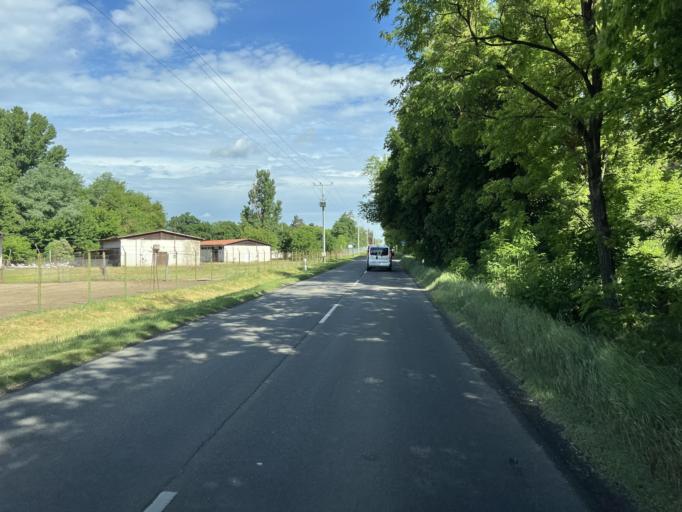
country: HU
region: Pest
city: Godollo
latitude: 47.5634
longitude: 19.3758
